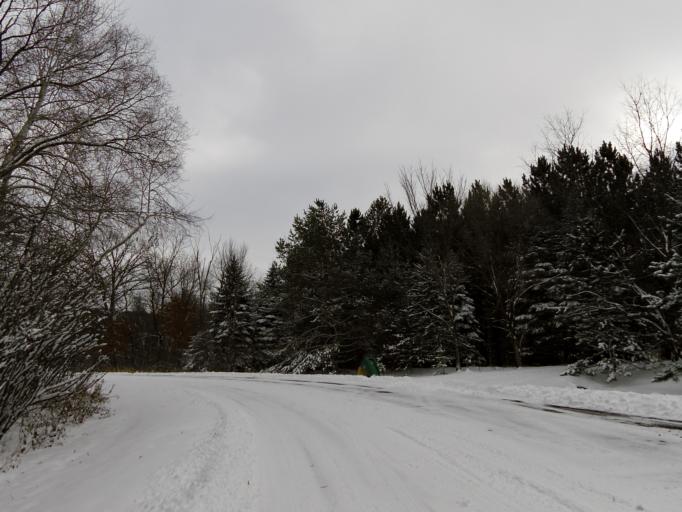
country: US
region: Minnesota
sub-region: Washington County
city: Lake Elmo
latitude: 44.9717
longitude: -92.8333
